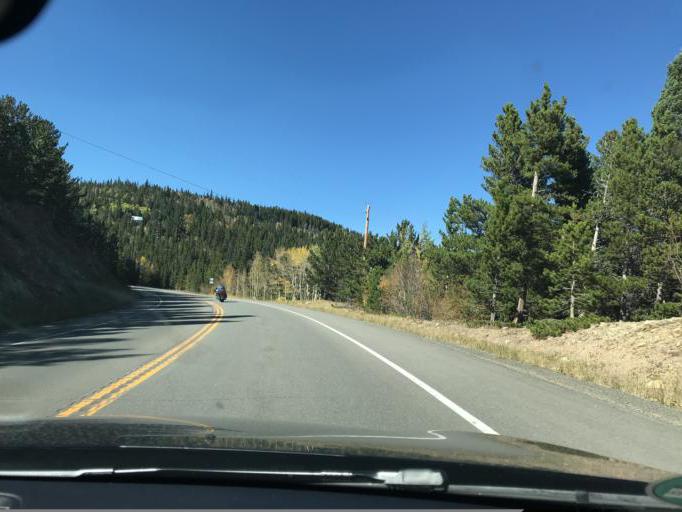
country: US
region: Colorado
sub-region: Boulder County
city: Nederland
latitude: 40.0710
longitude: -105.5110
